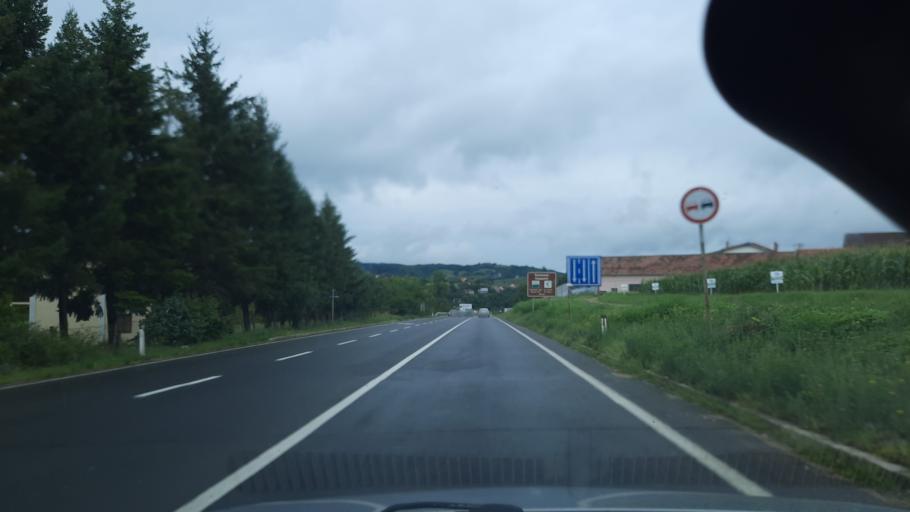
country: RS
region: Central Serbia
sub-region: Sumadijski Okrug
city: Kragujevac
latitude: 43.9802
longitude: 20.8294
